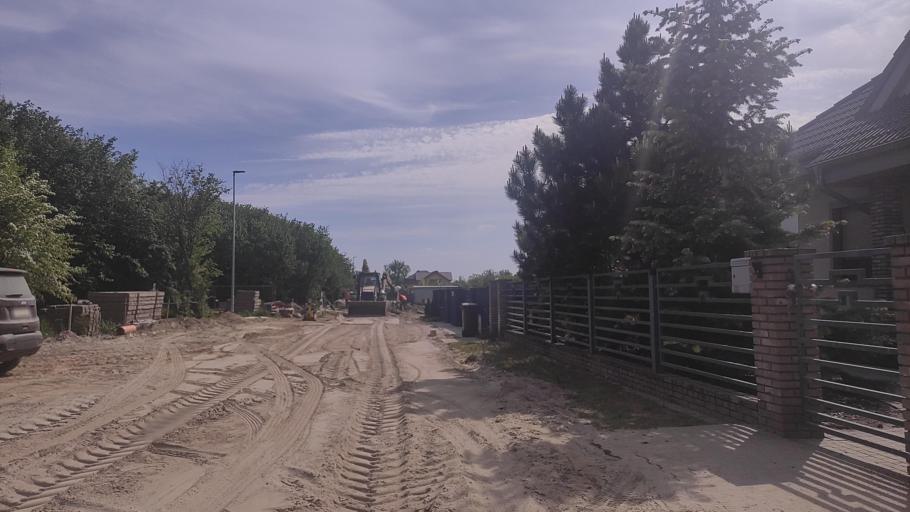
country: PL
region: Greater Poland Voivodeship
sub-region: Powiat poznanski
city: Swarzedz
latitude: 52.4117
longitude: 17.1053
